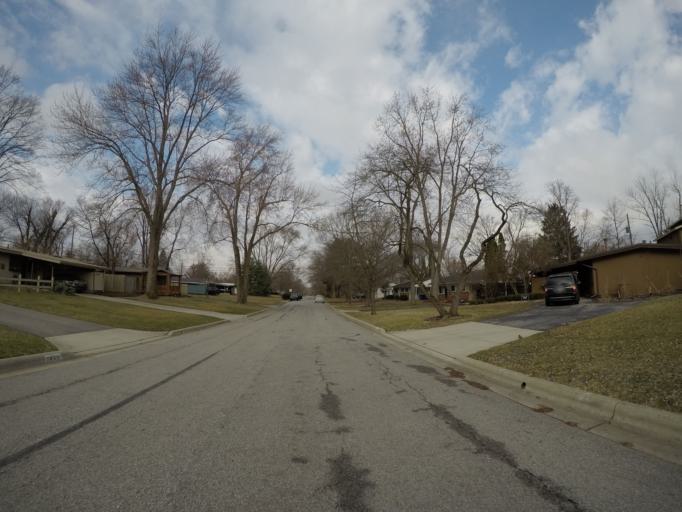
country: US
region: Ohio
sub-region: Franklin County
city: Upper Arlington
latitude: 40.0289
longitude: -83.0821
